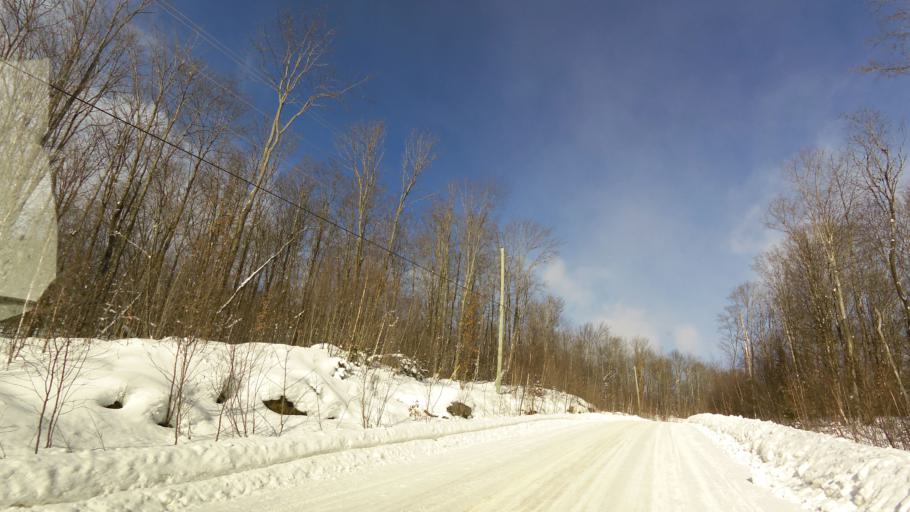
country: CA
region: Ontario
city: Bancroft
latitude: 45.0537
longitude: -78.5340
